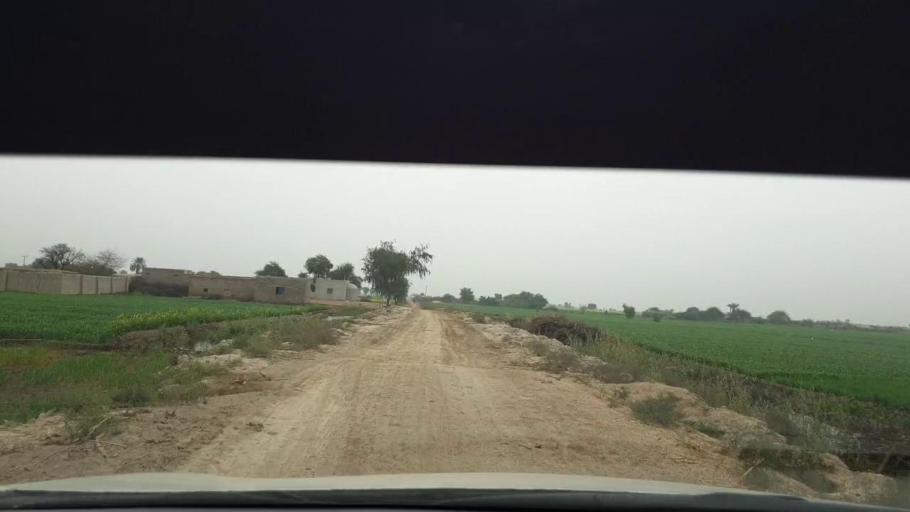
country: PK
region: Sindh
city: Berani
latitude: 25.7570
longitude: 68.8528
